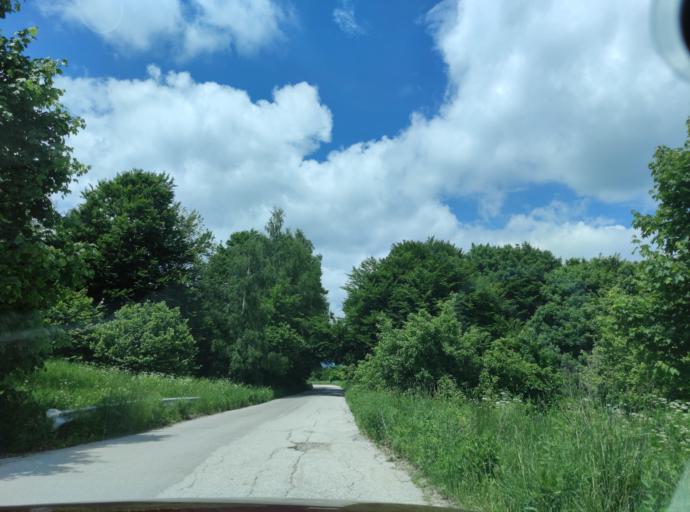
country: BG
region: Sofia-Capital
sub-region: Stolichna Obshtina
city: Sofia
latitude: 42.6339
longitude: 23.2394
